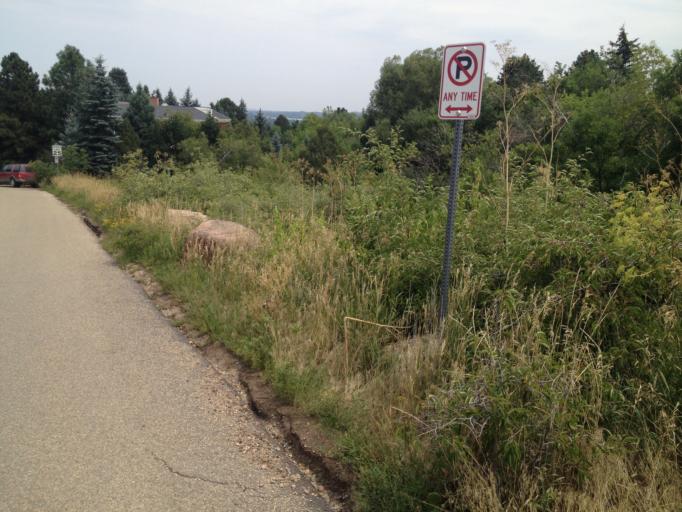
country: US
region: Colorado
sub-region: Boulder County
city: Boulder
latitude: 39.9986
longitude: -105.2784
